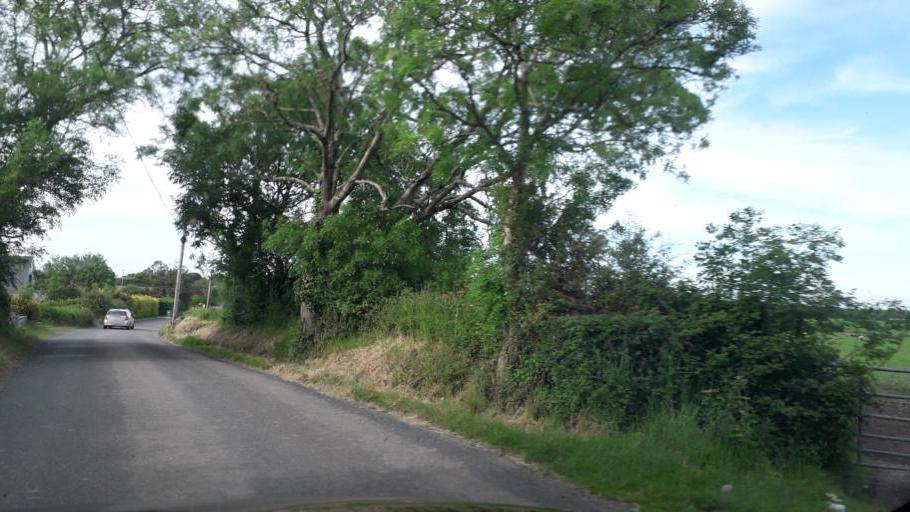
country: IE
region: Leinster
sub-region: Loch Garman
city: Courtown
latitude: 52.5224
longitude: -6.2722
